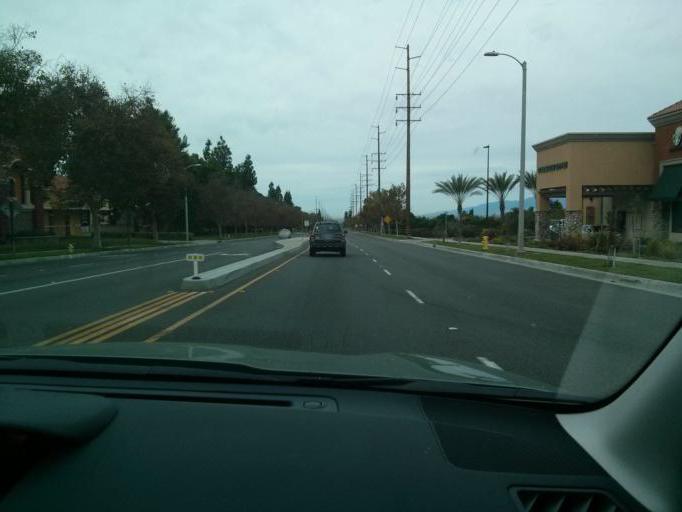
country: US
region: California
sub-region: San Bernardino County
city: Mentone
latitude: 34.0702
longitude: -117.1402
